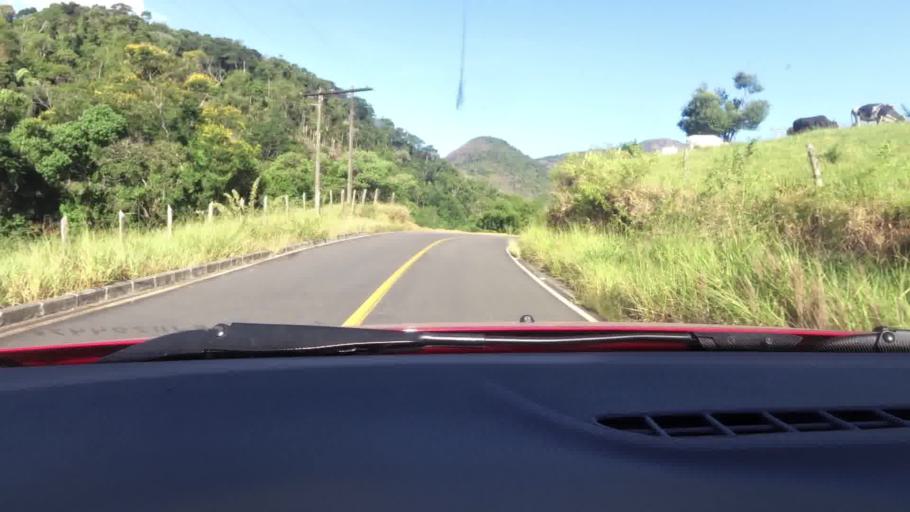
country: BR
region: Espirito Santo
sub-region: Guarapari
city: Guarapari
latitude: -20.5740
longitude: -40.5432
